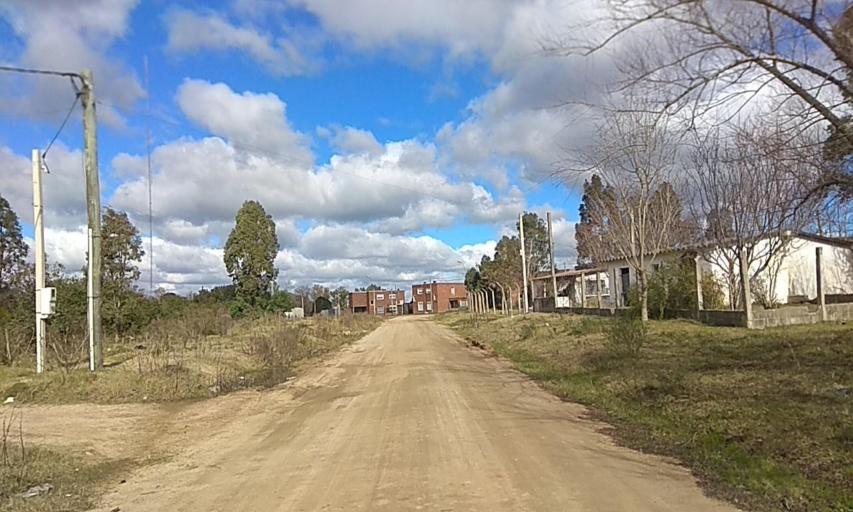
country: UY
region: Florida
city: Florida
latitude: -34.0958
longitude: -56.2327
